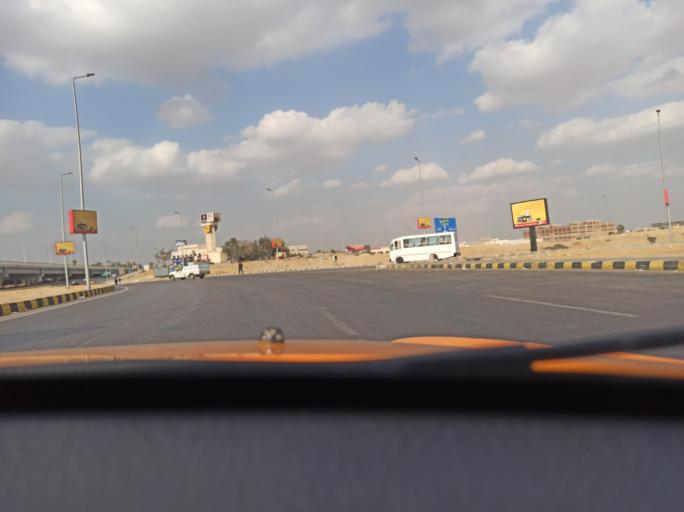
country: EG
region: Eastern Province
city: Bilbays
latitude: 30.2399
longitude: 31.7205
